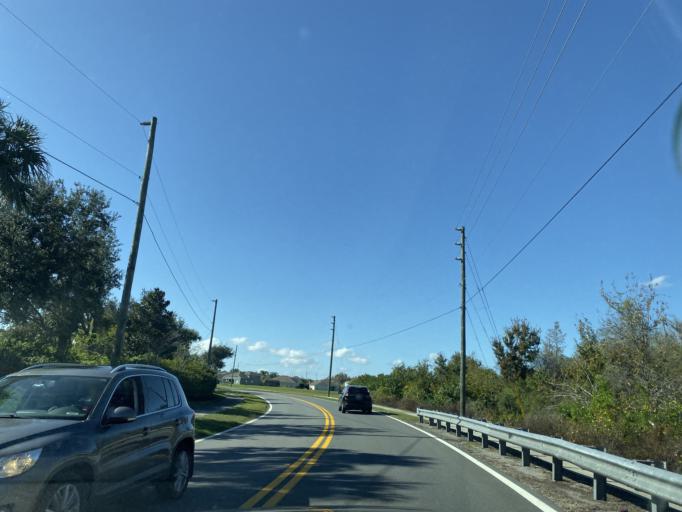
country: US
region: Florida
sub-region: Orange County
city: Meadow Woods
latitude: 28.3998
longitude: -81.2314
